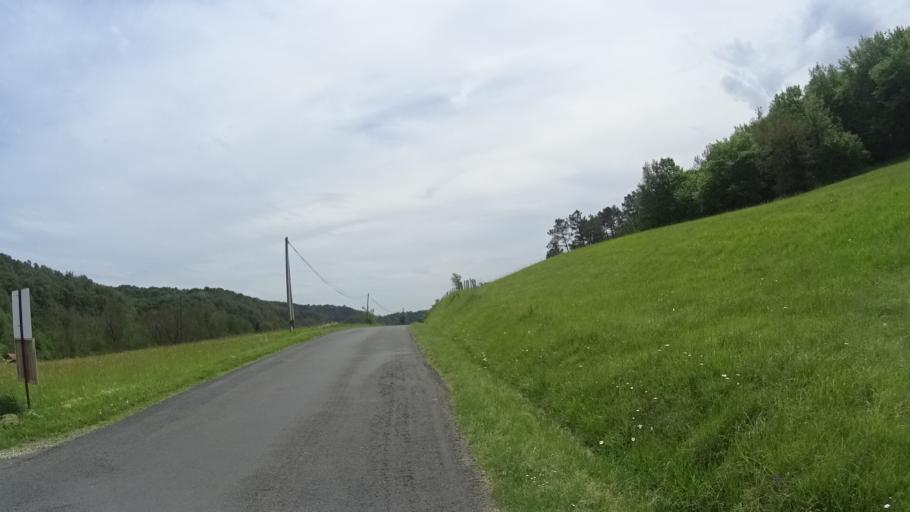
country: FR
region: Aquitaine
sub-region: Departement de la Dordogne
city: Sourzac
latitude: 45.0115
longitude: 0.4543
